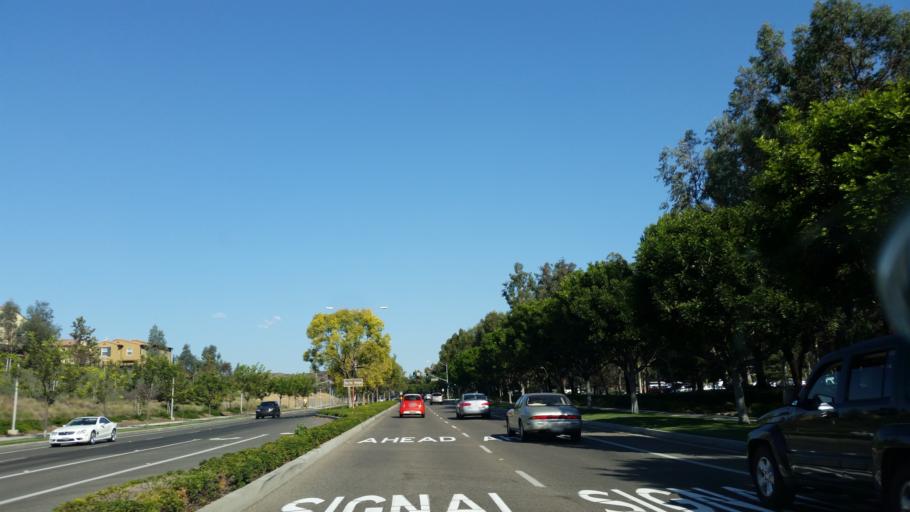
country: US
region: California
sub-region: Orange County
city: San Joaquin Hills
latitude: 33.6336
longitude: -117.8327
